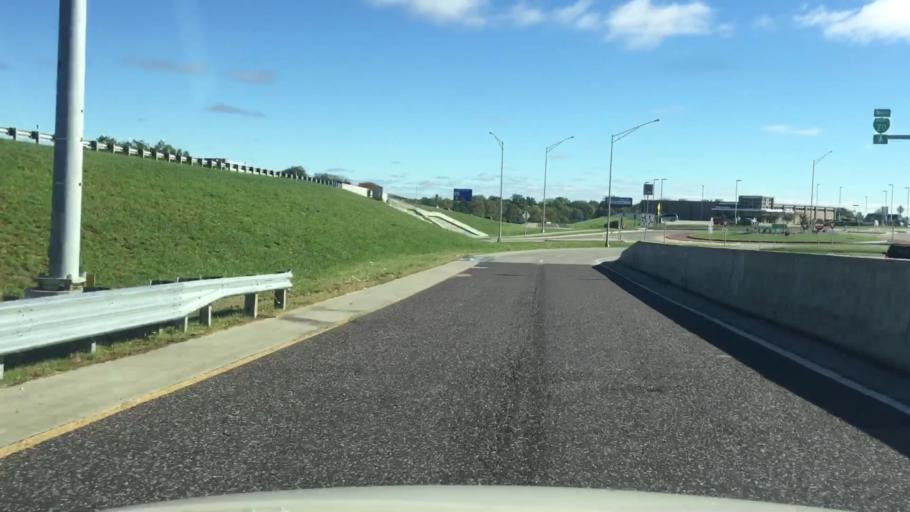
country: US
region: Missouri
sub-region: Boone County
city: Columbia
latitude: 38.9660
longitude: -92.3518
